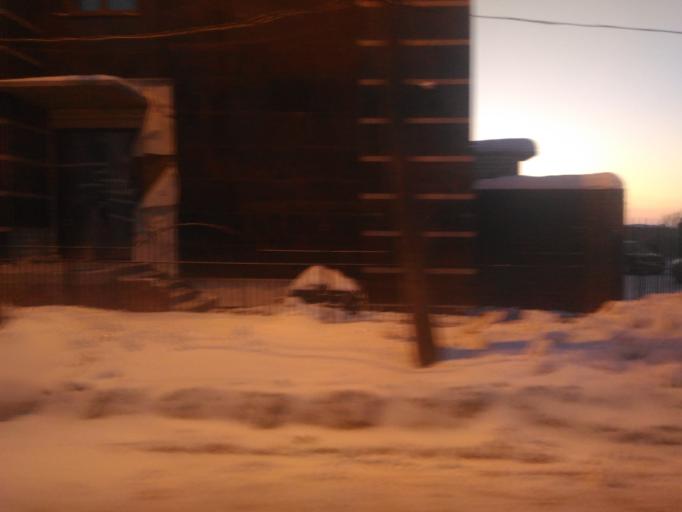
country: RU
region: Ulyanovsk
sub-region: Ulyanovskiy Rayon
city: Ulyanovsk
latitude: 54.3150
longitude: 48.3860
